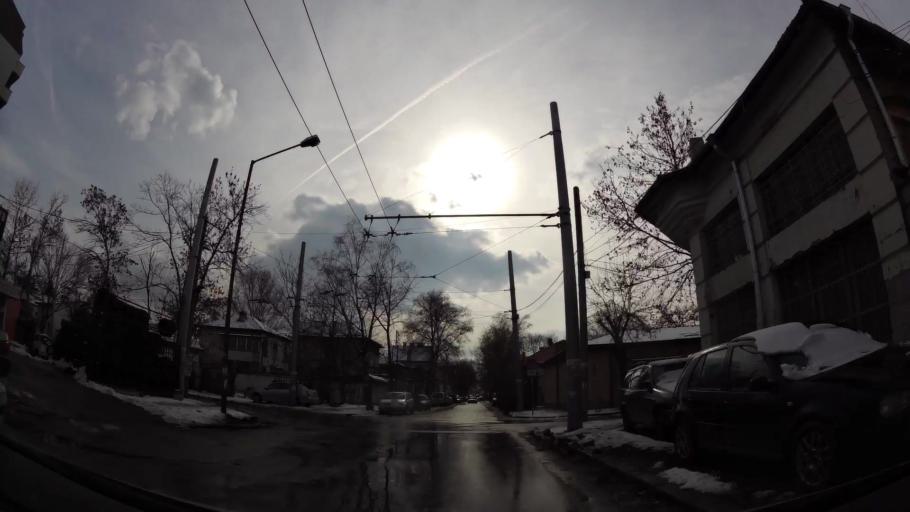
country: BG
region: Sofia-Capital
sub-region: Stolichna Obshtina
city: Sofia
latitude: 42.7031
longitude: 23.3462
